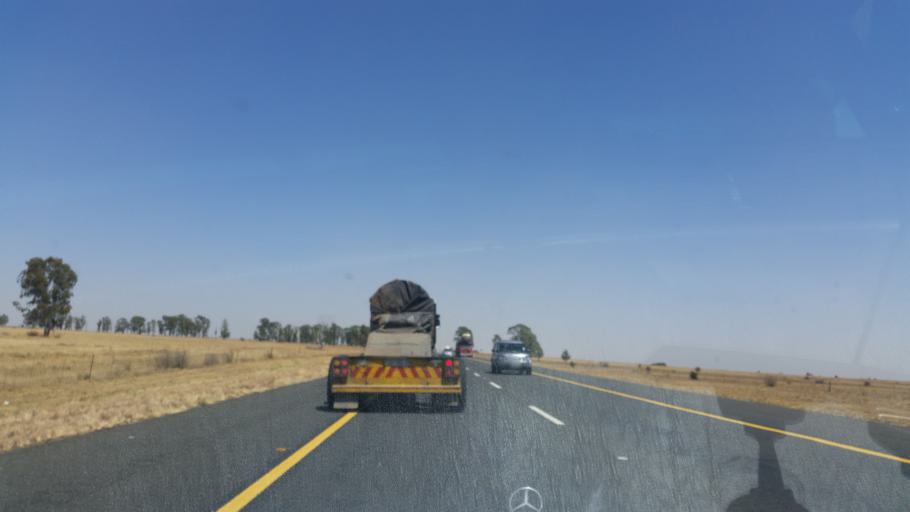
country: ZA
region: Orange Free State
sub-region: Lejweleputswa District Municipality
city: Winburg
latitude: -28.6387
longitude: 26.8931
